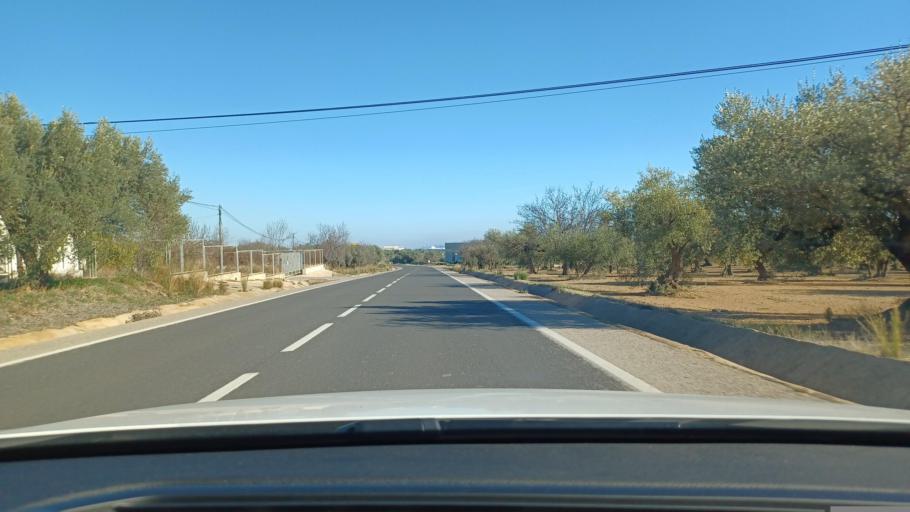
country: ES
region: Valencia
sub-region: Provincia de Castello
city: Rosell
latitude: 40.6306
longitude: 0.2994
